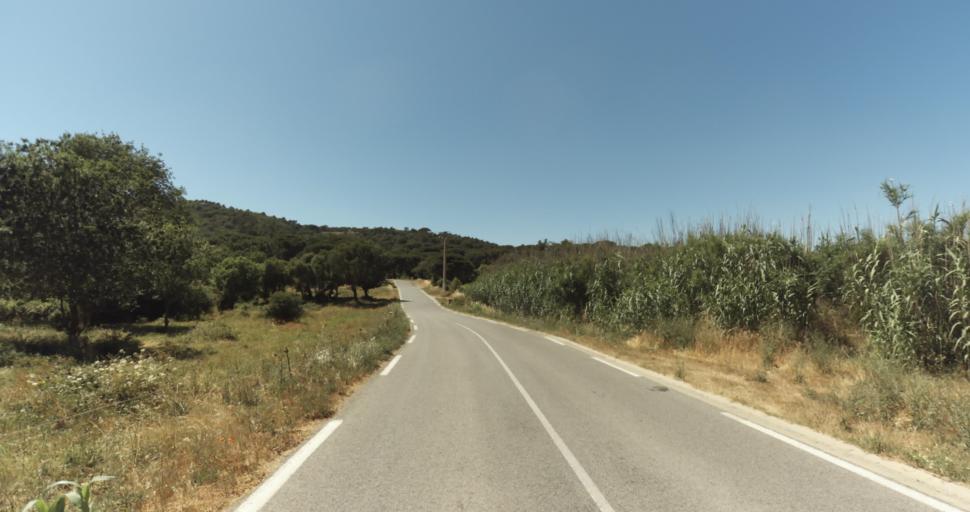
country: FR
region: Provence-Alpes-Cote d'Azur
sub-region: Departement du Var
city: Gassin
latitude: 43.2390
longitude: 6.5682
